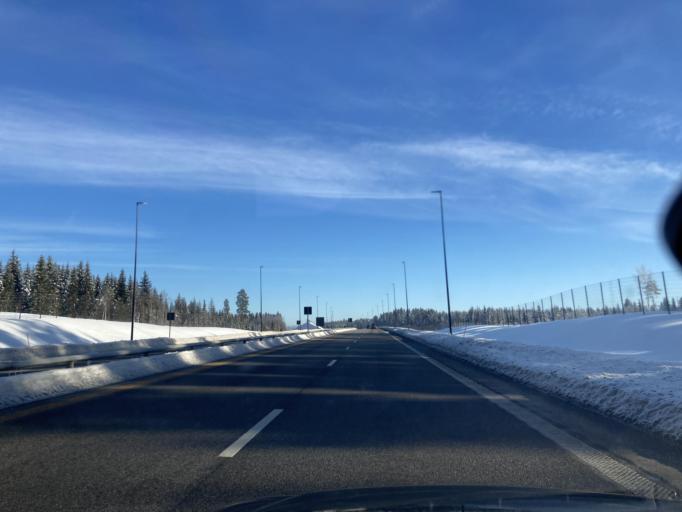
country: NO
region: Hedmark
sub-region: Loten
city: Loten
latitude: 60.8516
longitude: 11.3833
